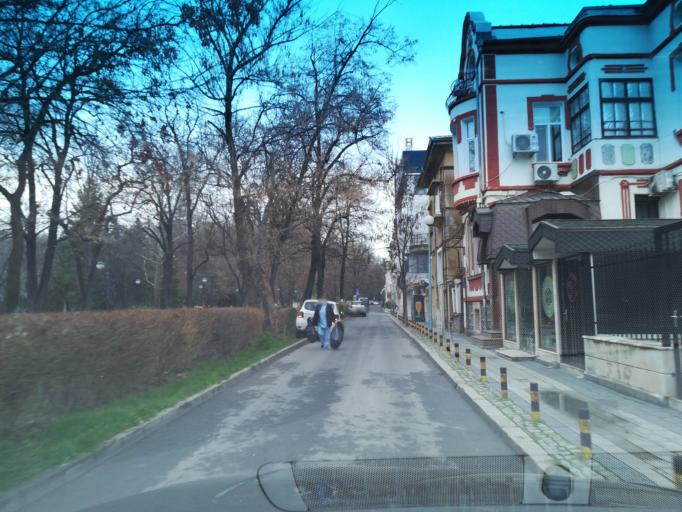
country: BG
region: Plovdiv
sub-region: Obshtina Plovdiv
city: Plovdiv
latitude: 42.1399
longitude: 24.7461
